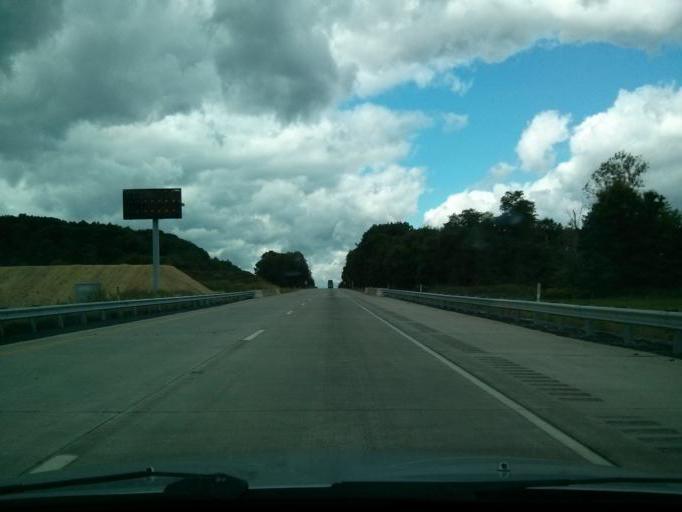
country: US
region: Pennsylvania
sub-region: Jefferson County
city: Reynoldsville
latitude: 41.1525
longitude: -78.9091
